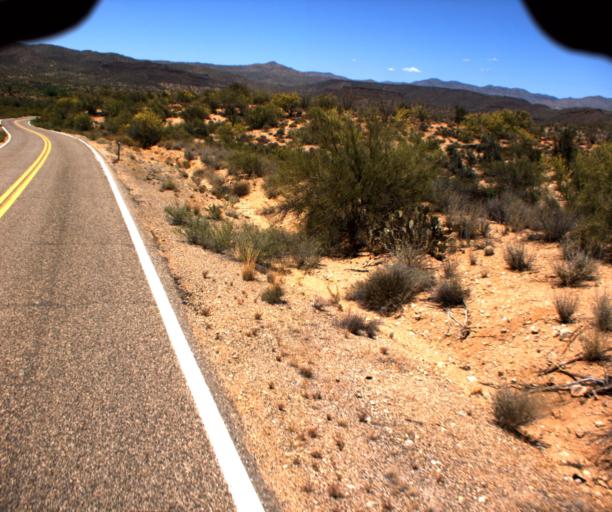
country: US
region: Arizona
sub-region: Yavapai County
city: Bagdad
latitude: 34.4691
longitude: -113.0499
